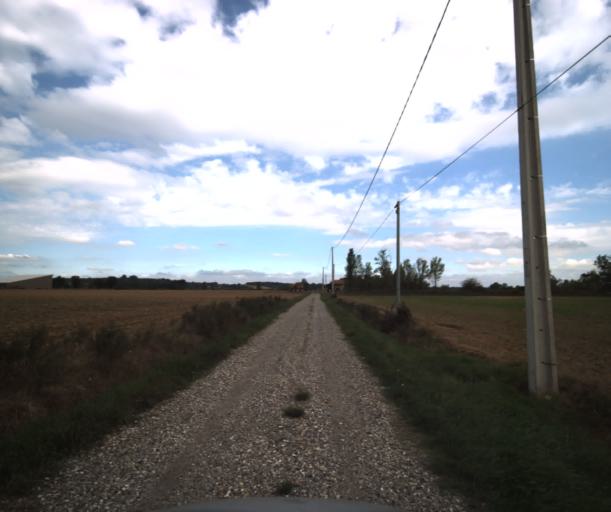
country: FR
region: Midi-Pyrenees
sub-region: Departement de la Haute-Garonne
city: Lherm
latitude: 43.3930
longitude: 1.2307
